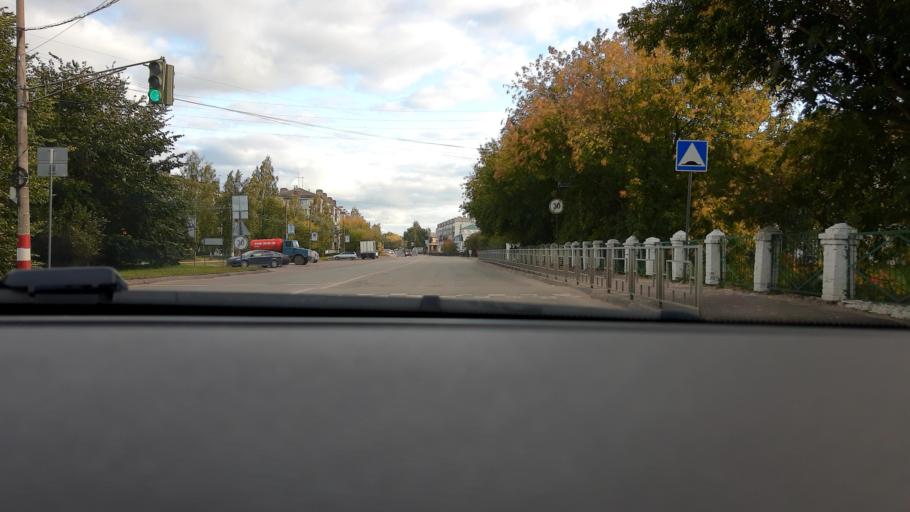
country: RU
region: Nizjnij Novgorod
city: Novaya Balakhna
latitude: 56.4994
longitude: 43.6048
